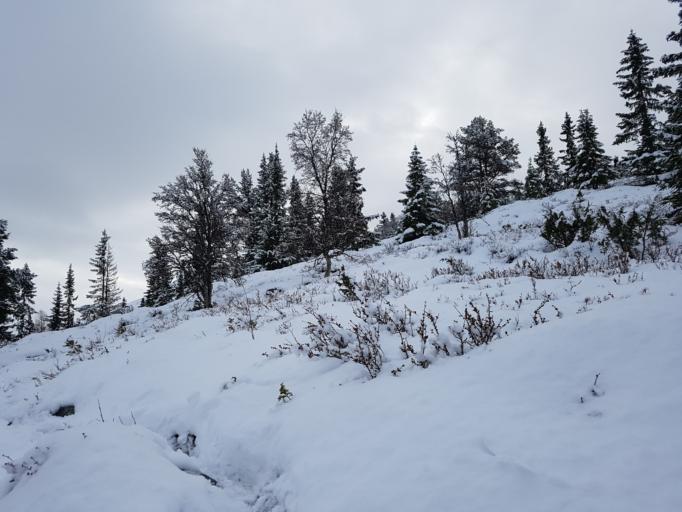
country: NO
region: Oppland
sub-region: Sel
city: Otta
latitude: 61.8062
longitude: 9.6779
